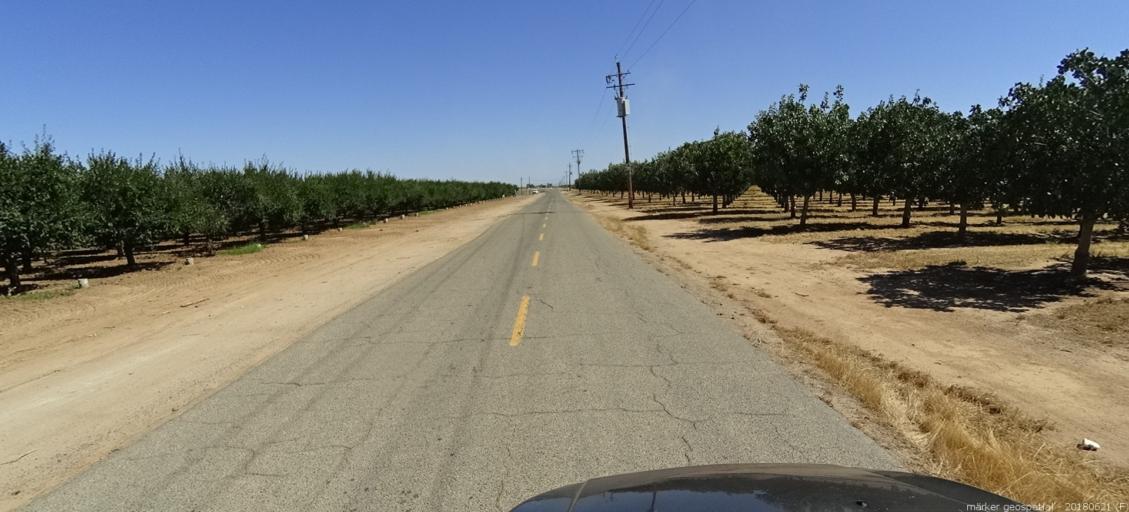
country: US
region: California
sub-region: Madera County
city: Parksdale
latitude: 36.9072
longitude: -119.9394
